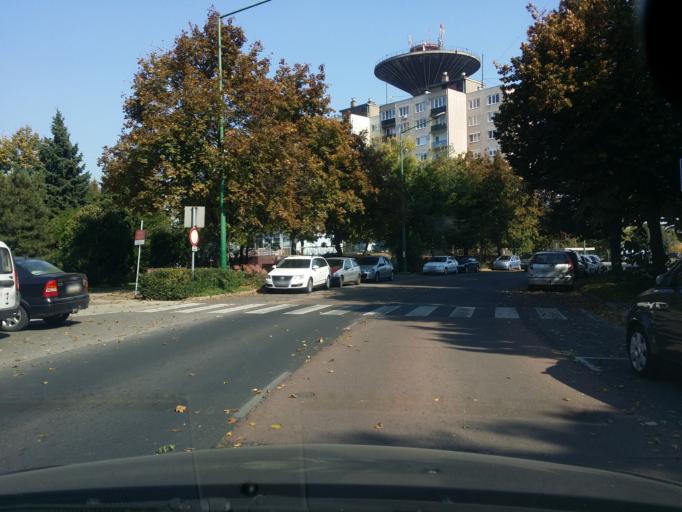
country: HU
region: Fejer
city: dunaujvaros
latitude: 46.9735
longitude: 18.9333
